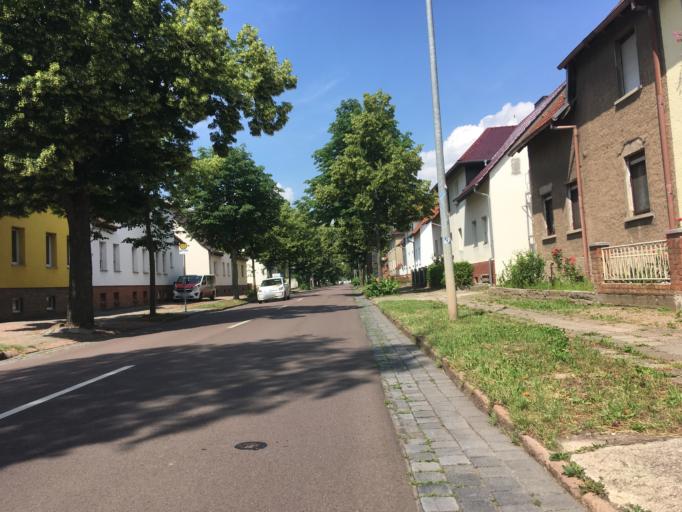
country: DE
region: Saxony-Anhalt
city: Koethen
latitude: 51.7529
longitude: 12.0086
